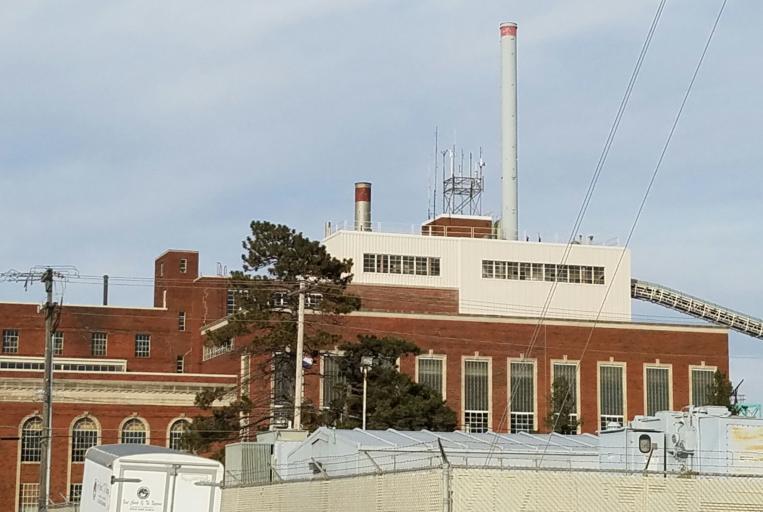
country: US
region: Missouri
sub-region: Saline County
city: Marshall
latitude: 39.1205
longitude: -93.2090
